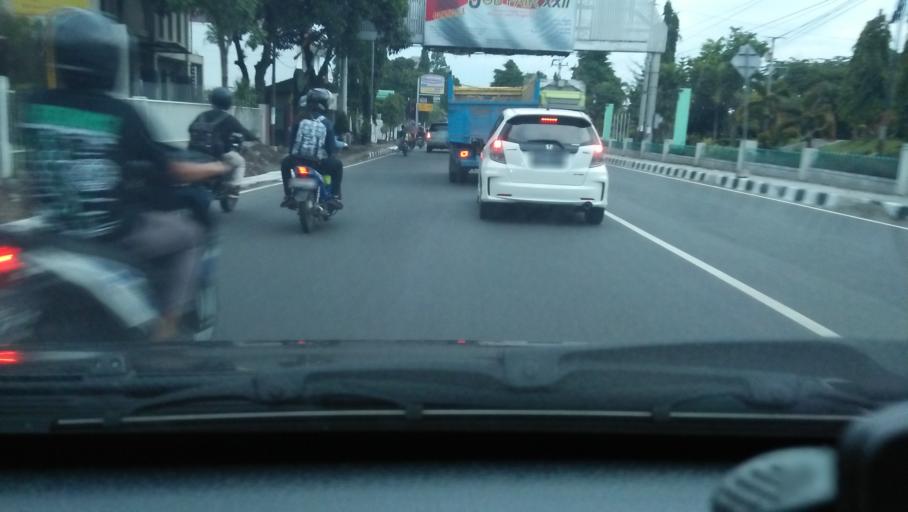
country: ID
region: Central Java
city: Magelang
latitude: -7.4596
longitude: 110.2227
